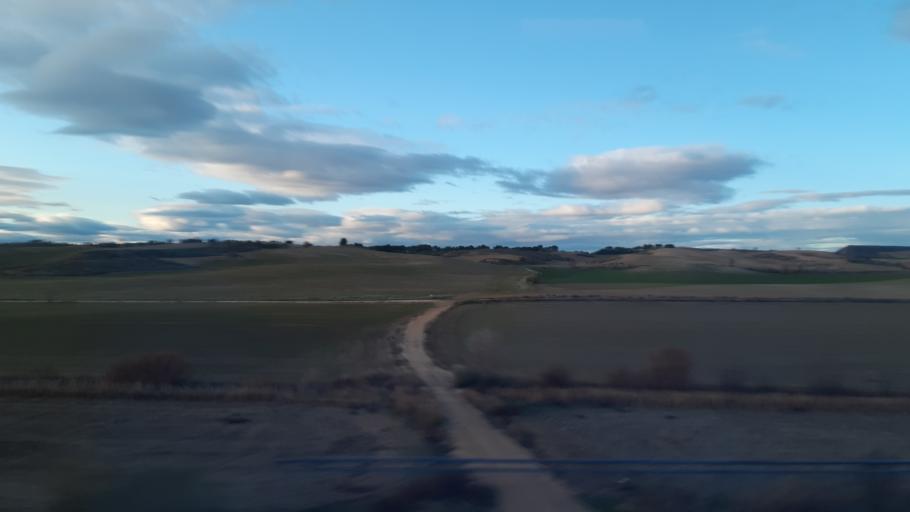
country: ES
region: Madrid
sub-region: Provincia de Madrid
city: Villalbilla
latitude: 40.4511
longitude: -3.3243
